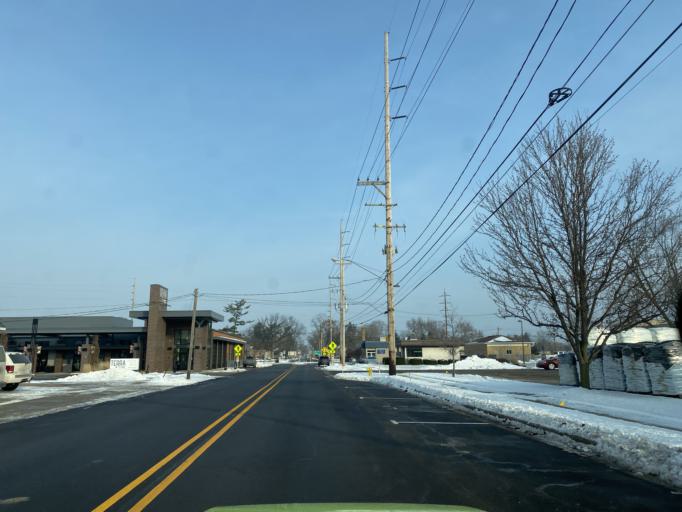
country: US
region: Michigan
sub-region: Ottawa County
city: Hudsonville
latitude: 42.8670
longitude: -85.8651
